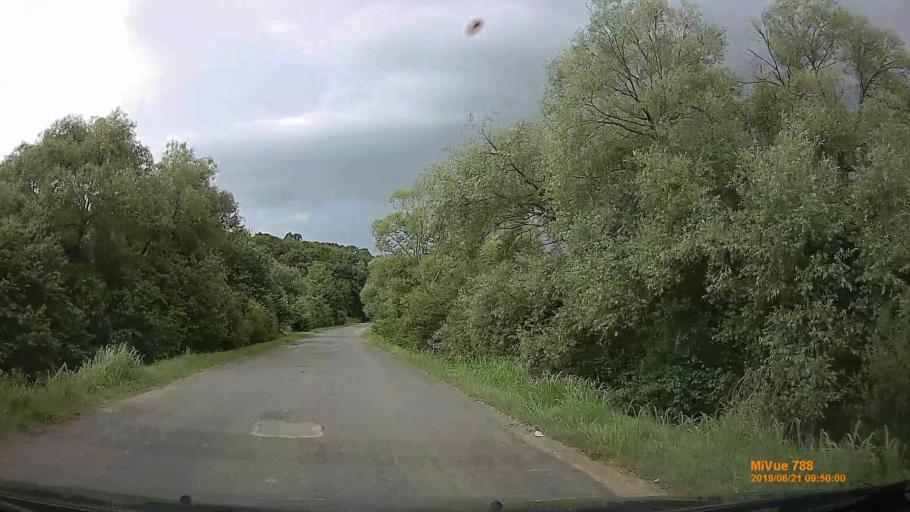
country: HU
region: Baranya
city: Sasd
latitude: 46.2634
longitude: 18.0348
